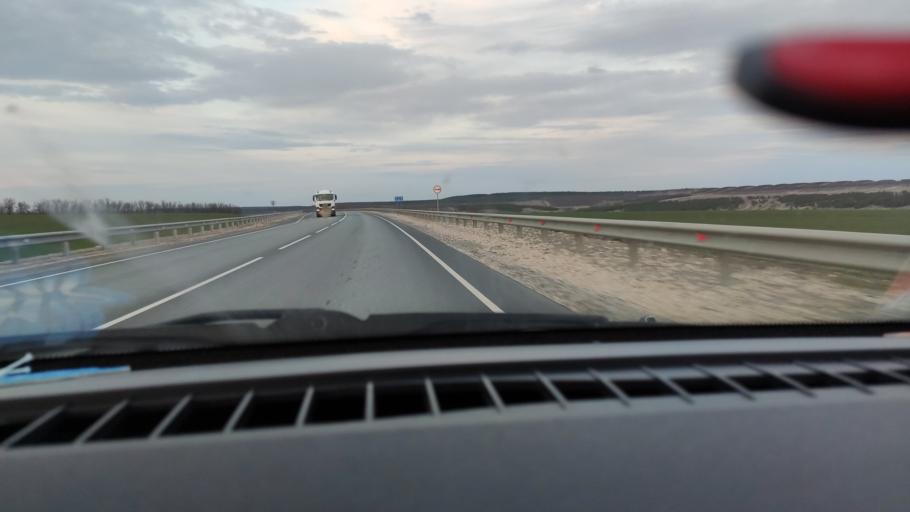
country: RU
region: Saratov
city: Yelshanka
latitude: 51.8363
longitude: 46.4724
